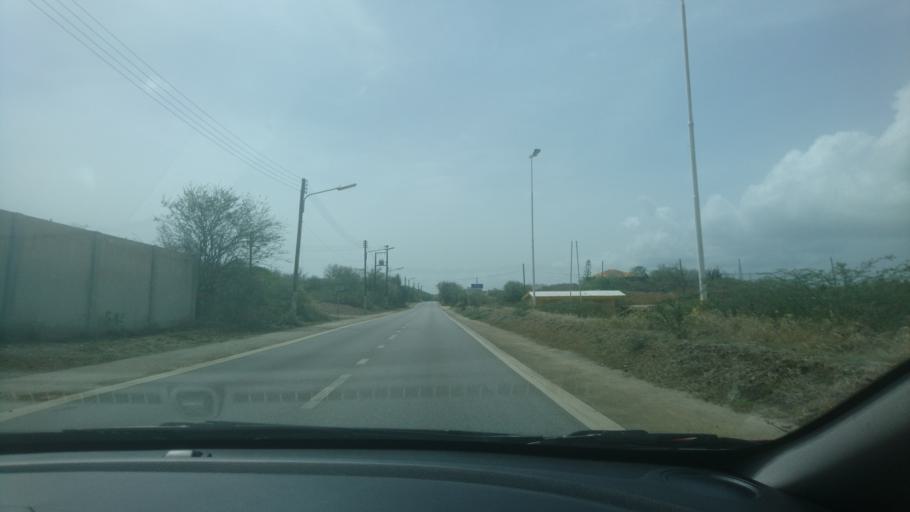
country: CW
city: Dorp Soto
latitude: 12.2739
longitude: -69.1074
